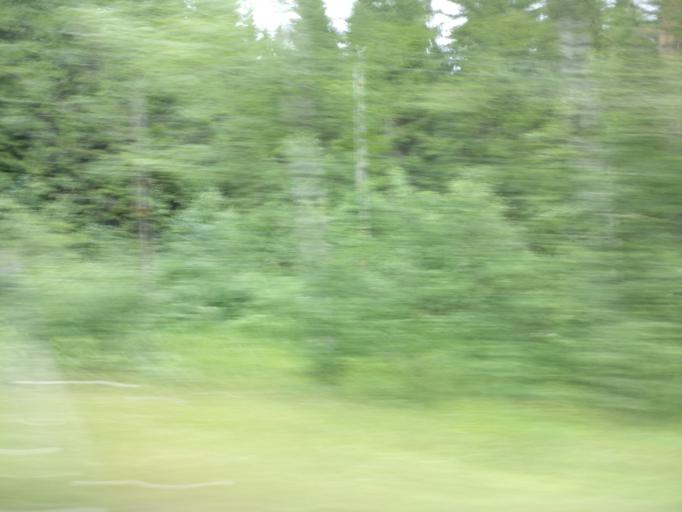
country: FI
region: Northern Savo
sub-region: Varkaus
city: Kangaslampi
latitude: 62.1647
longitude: 28.1395
